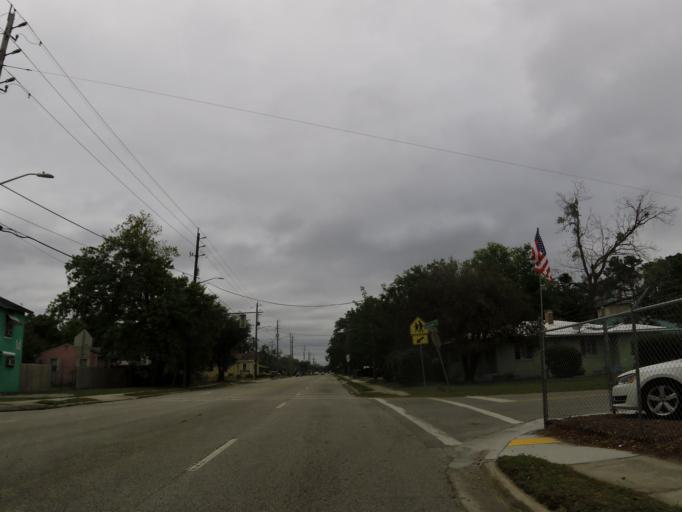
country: US
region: Florida
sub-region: Duval County
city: Jacksonville
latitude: 30.2807
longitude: -81.6437
